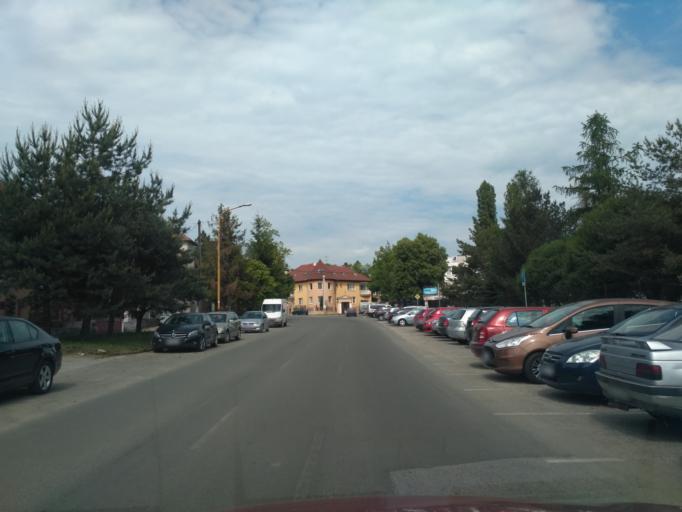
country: SK
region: Kosicky
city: Kosice
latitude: 48.7286
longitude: 21.2388
